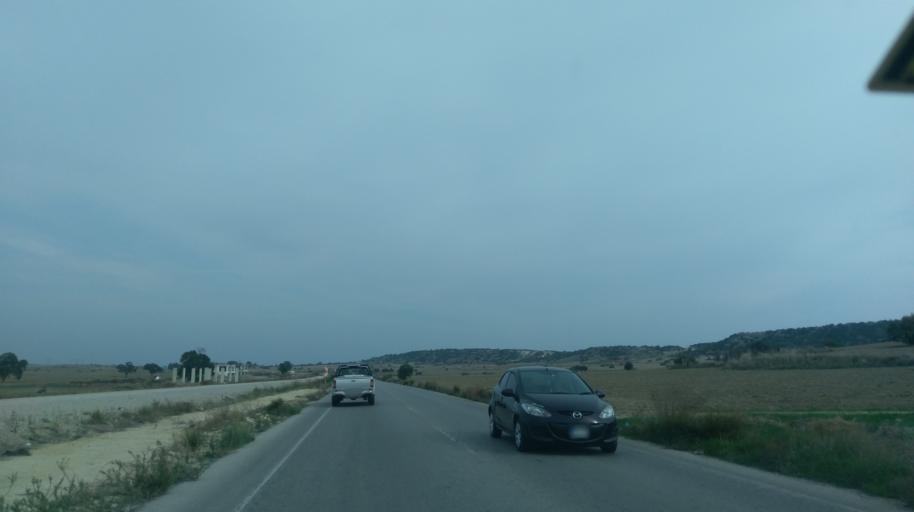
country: CY
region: Ammochostos
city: Trikomo
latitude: 35.3533
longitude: 34.0019
